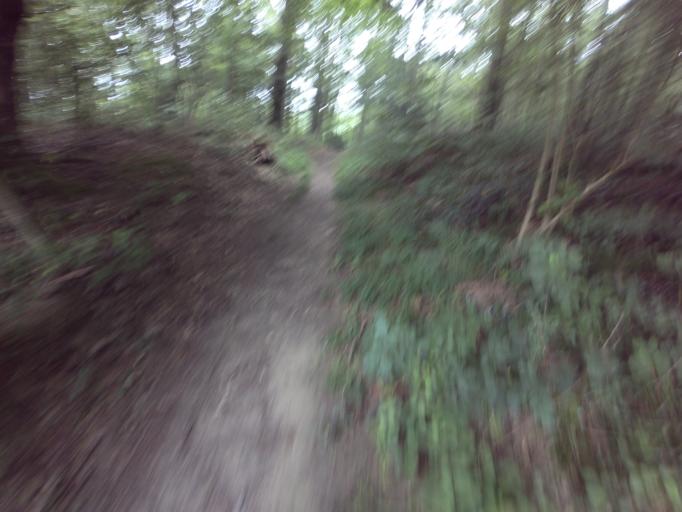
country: BE
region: Wallonia
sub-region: Province de Liege
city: Plombieres
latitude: 50.7749
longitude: 5.9330
